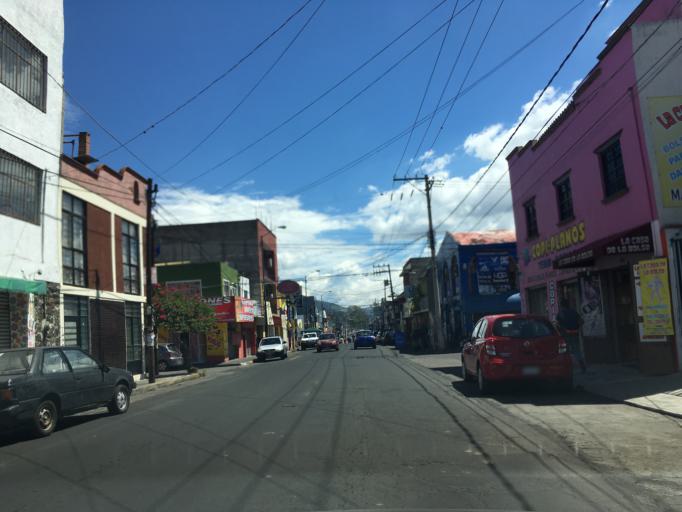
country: MX
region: Michoacan
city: Morelia
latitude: 19.6902
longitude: -101.2001
